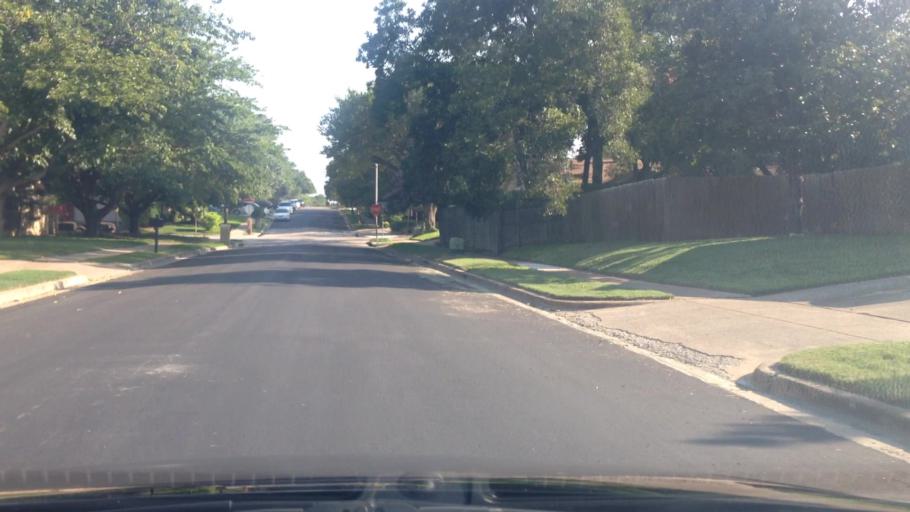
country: US
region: Texas
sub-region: Tarrant County
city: Edgecliff Village
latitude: 32.6534
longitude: -97.3402
